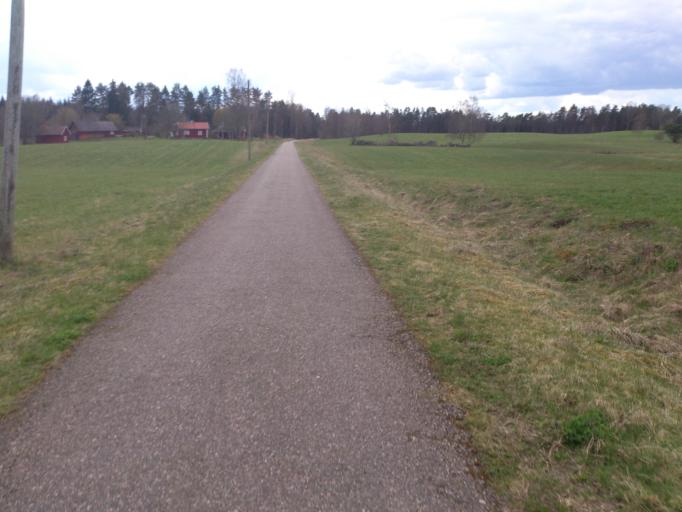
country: SE
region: Vaestra Goetaland
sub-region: Falkopings Kommun
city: Falkoeping
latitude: 57.9794
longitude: 13.5232
